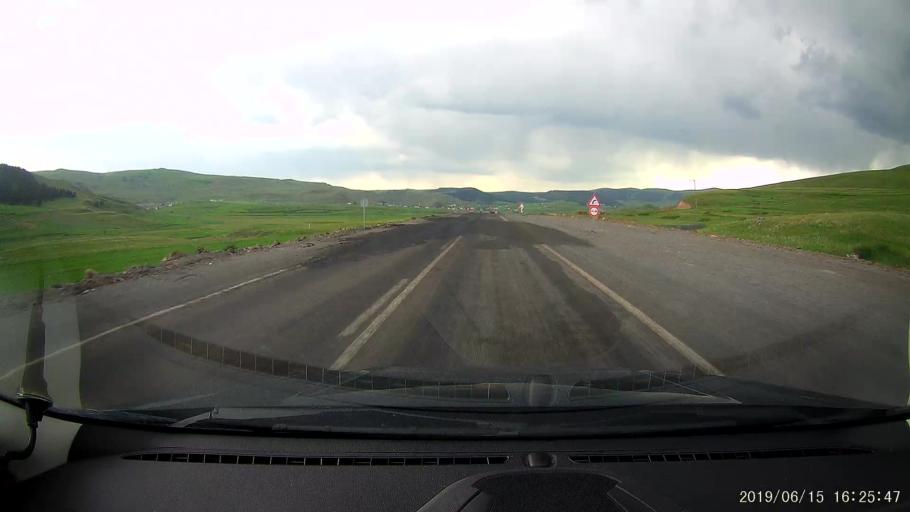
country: TR
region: Ardahan
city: Hanak
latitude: 41.1493
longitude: 42.8667
